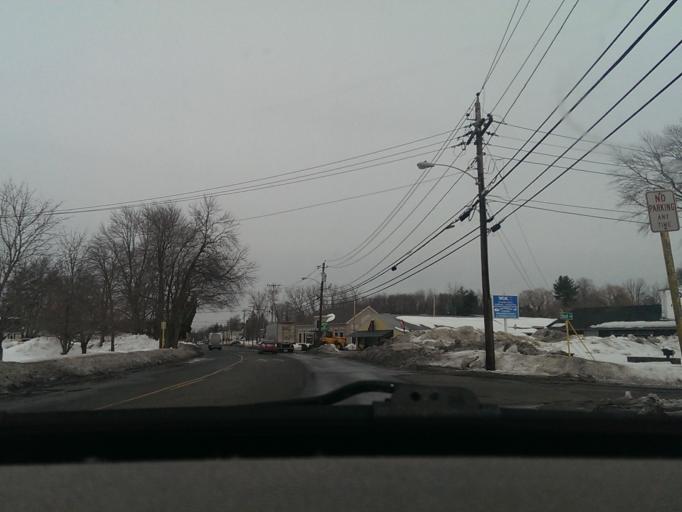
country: US
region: Massachusetts
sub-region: Hampden County
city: East Longmeadow
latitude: 42.0594
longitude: -72.5159
